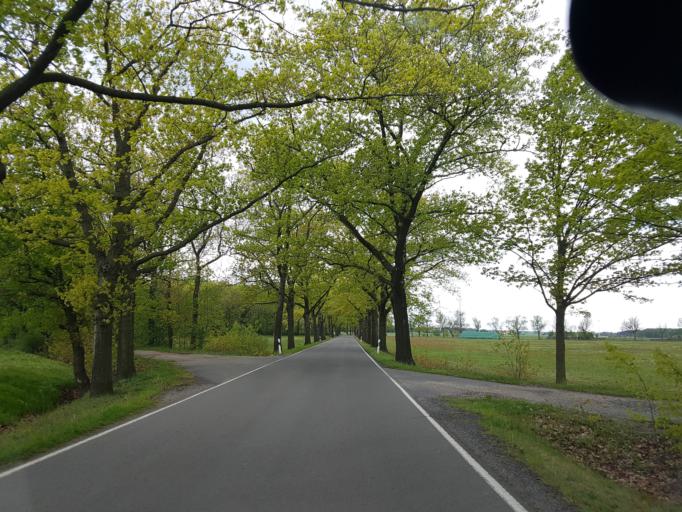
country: DE
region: Brandenburg
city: Bronkow
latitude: 51.6114
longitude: 13.9057
